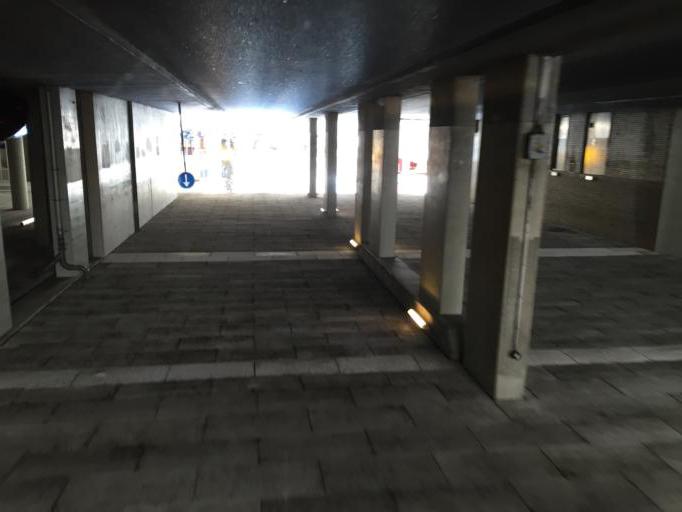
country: NL
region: South Holland
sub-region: Gemeente Zoetermeer
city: Zoetermeer
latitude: 52.0618
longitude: 4.4914
